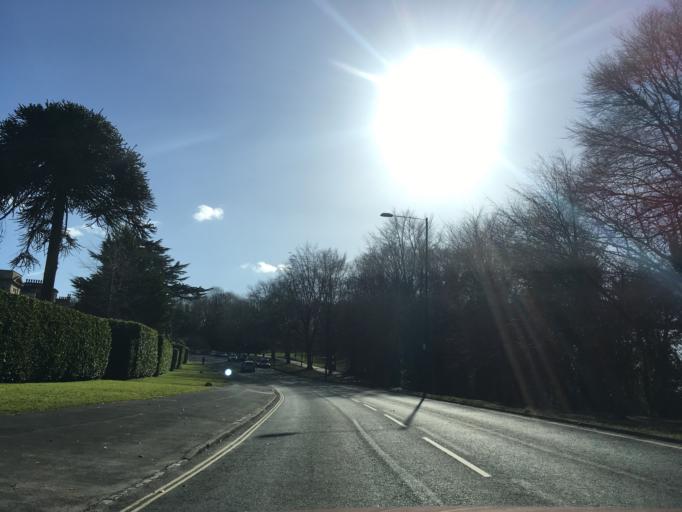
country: GB
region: England
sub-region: Bristol
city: Bristol
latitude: 51.4603
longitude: -2.6271
